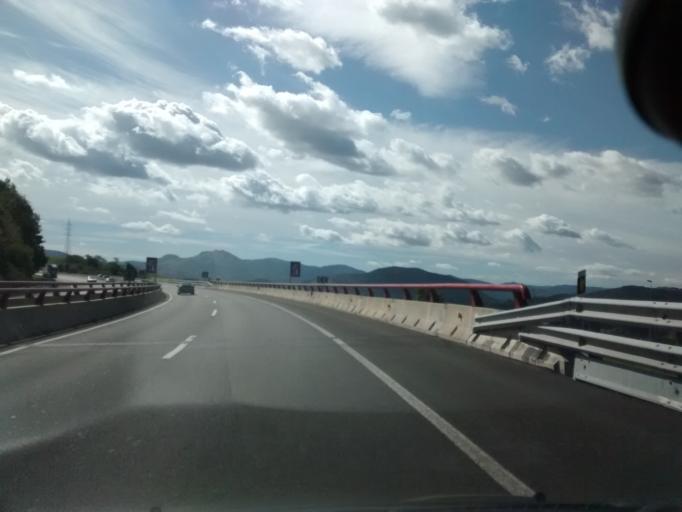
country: ES
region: Basque Country
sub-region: Provincia de Guipuzcoa
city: Usurbil
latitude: 43.2890
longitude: -2.0366
